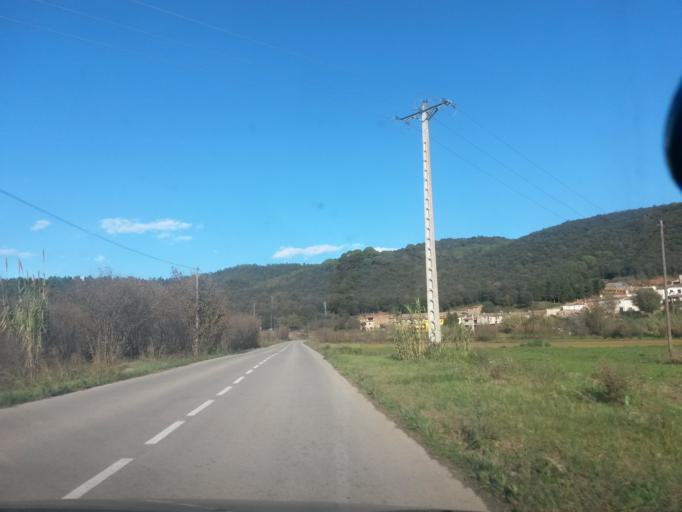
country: ES
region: Catalonia
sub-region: Provincia de Girona
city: Angles
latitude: 41.9640
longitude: 2.6435
